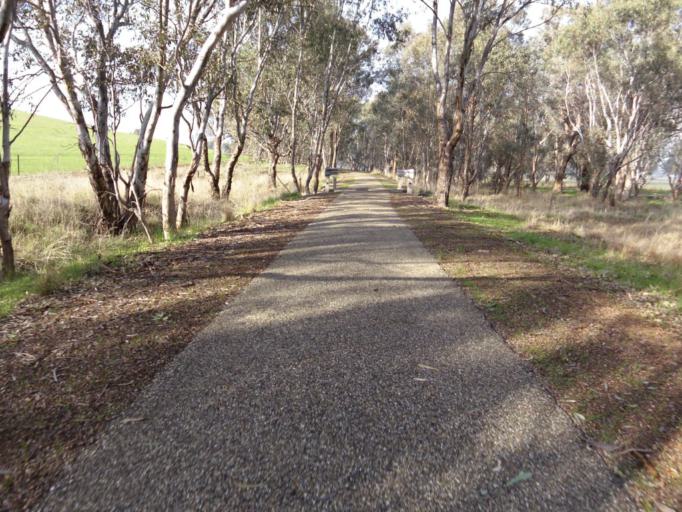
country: AU
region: Victoria
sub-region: Wangaratta
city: Wangaratta
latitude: -36.4471
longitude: 146.5513
